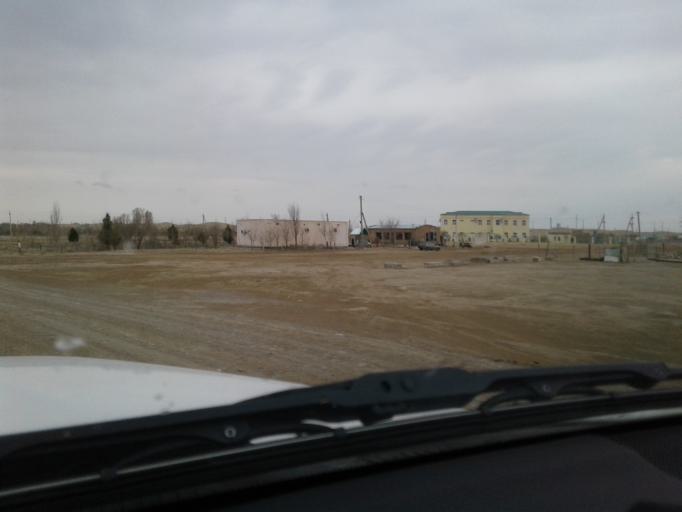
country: TM
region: Ahal
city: Abadan
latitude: 38.7581
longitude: 58.4913
